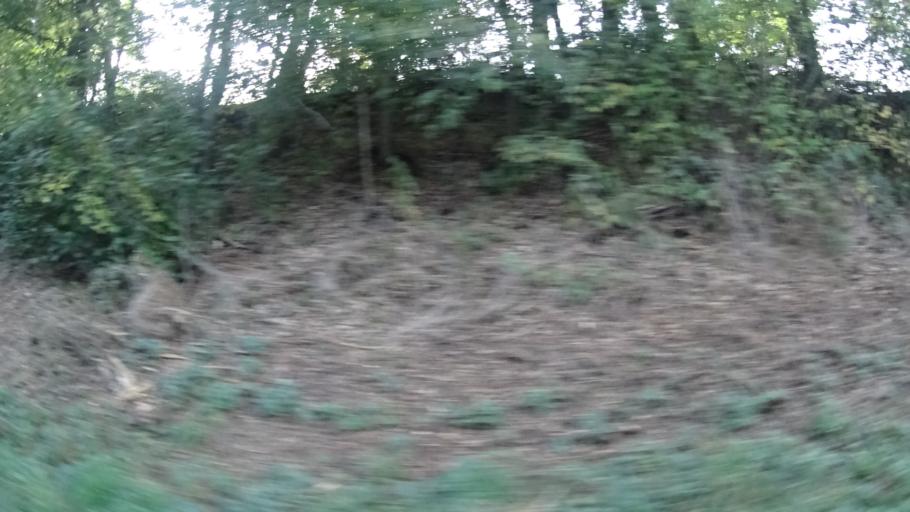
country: DE
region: Hesse
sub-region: Regierungsbezirk Kassel
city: Eichenzell
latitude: 50.5087
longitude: 9.6662
